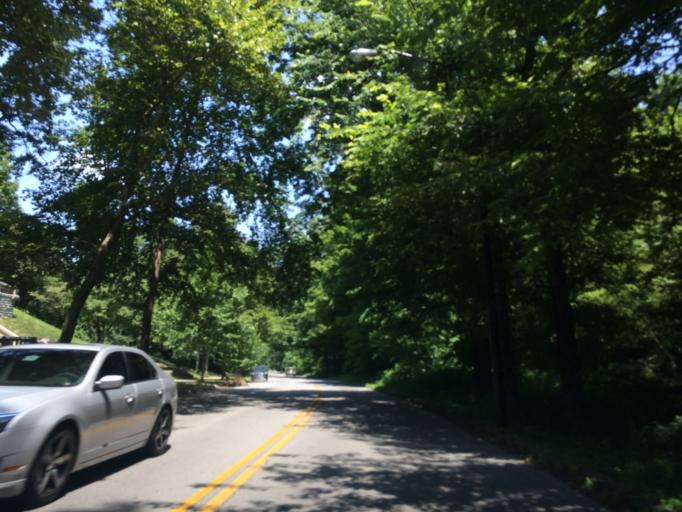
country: US
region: Kentucky
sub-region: Jefferson County
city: Audubon Park
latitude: 38.2386
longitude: -85.7070
